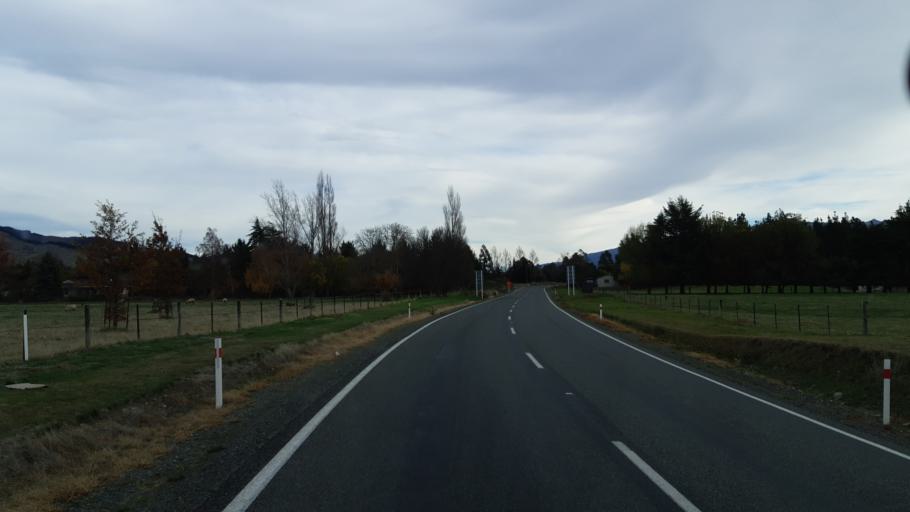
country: NZ
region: Tasman
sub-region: Tasman District
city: Brightwater
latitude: -41.6371
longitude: 173.3207
